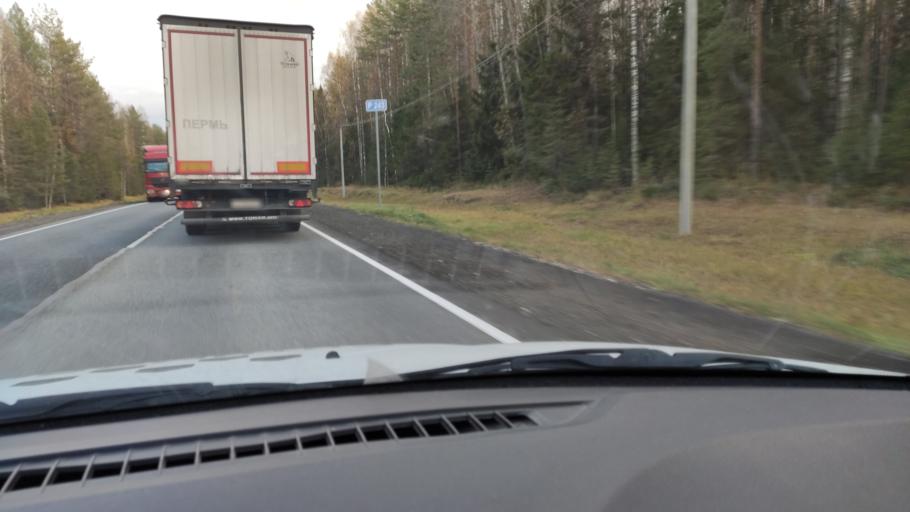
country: RU
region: Kirov
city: Dubrovka
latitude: 58.9096
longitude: 51.1763
